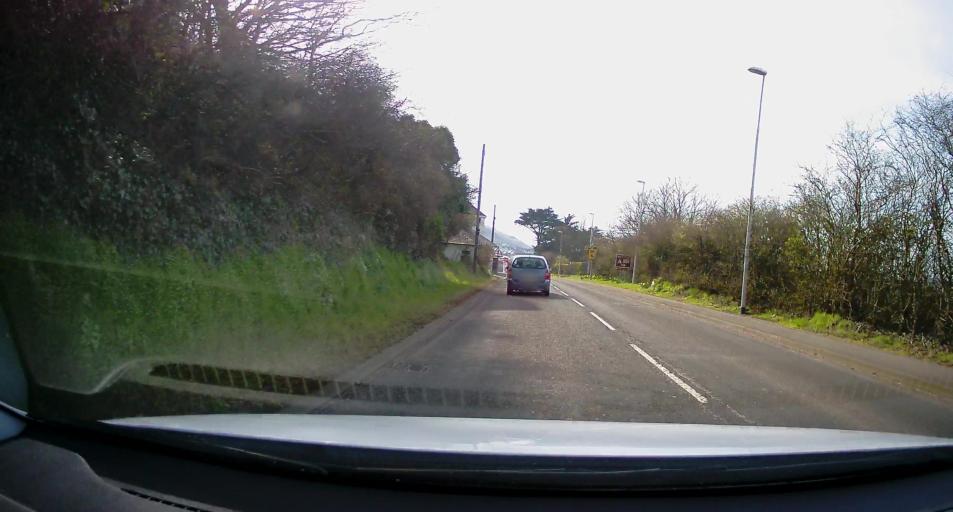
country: GB
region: Wales
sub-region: County of Ceredigion
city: Aberaeron
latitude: 52.2450
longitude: -4.2530
